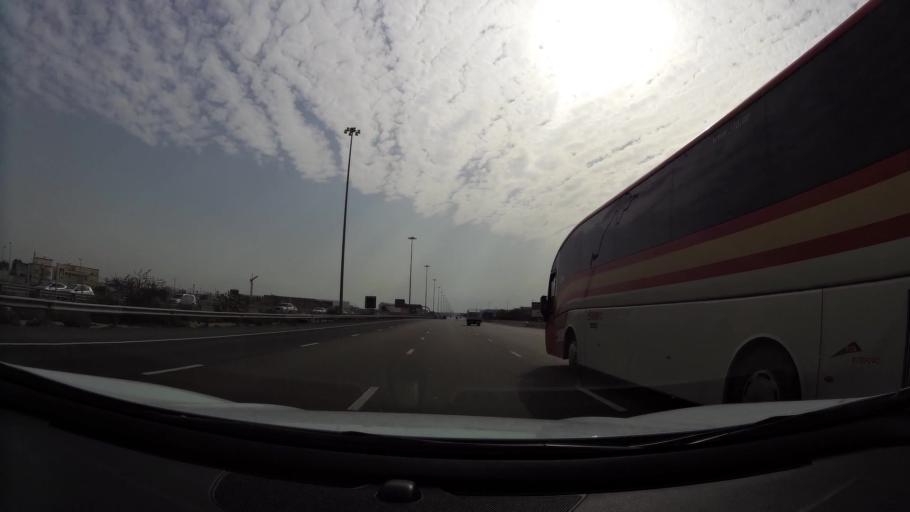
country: AE
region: Abu Dhabi
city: Abu Dhabi
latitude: 24.5391
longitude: 54.6854
